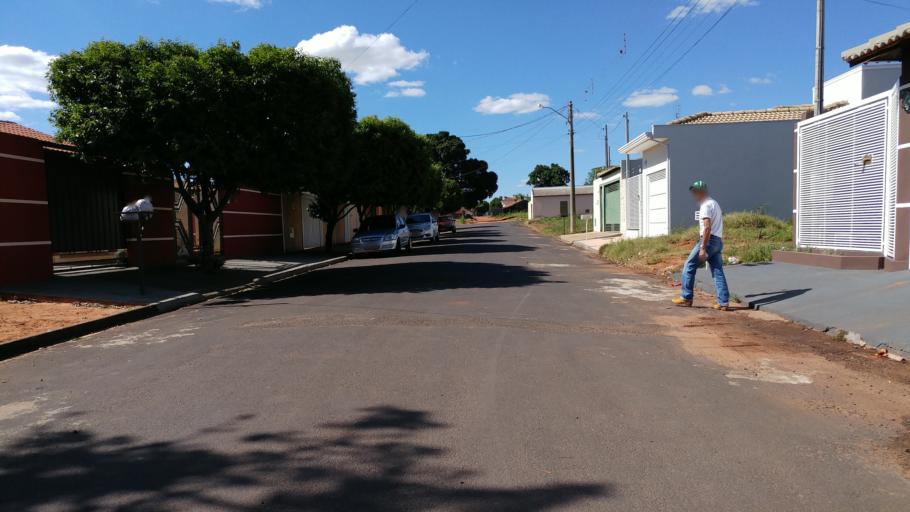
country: BR
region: Sao Paulo
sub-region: Paraguacu Paulista
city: Paraguacu Paulista
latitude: -22.4191
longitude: -50.5860
